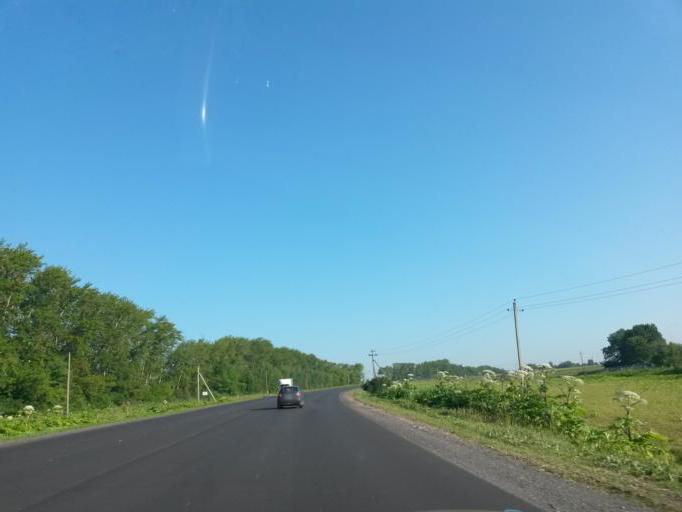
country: RU
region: Moskovskaya
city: Barybino
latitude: 55.2550
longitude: 37.8354
